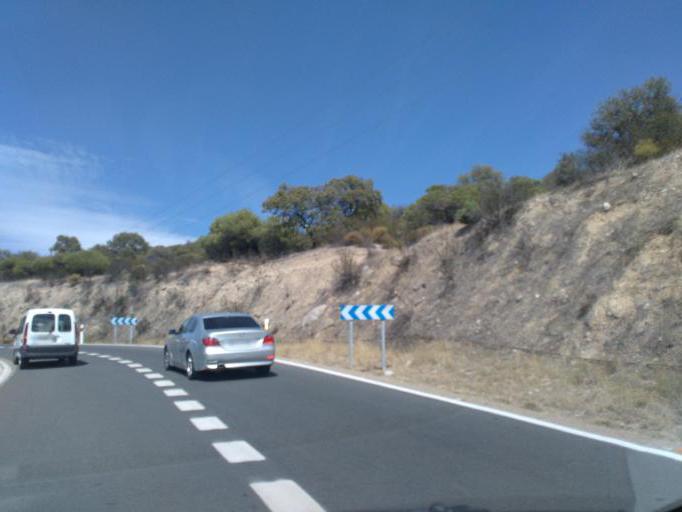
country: ES
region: Madrid
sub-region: Provincia de Madrid
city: Torrelodones
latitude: 40.5374
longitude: -3.9544
